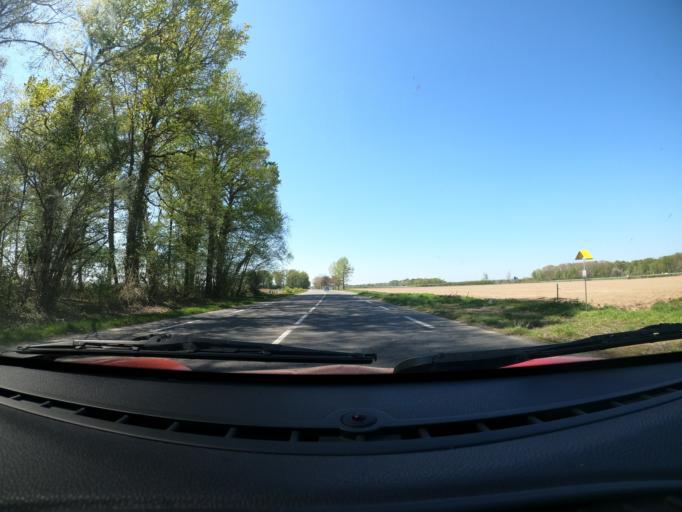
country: FR
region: Aquitaine
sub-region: Departement des Pyrenees-Atlantiques
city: Lescar
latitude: 43.3412
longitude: -0.4074
